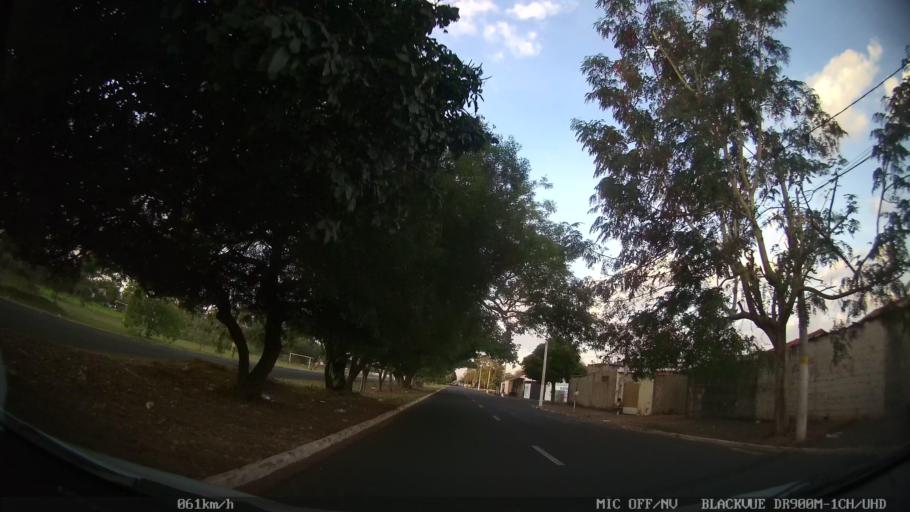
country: BR
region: Sao Paulo
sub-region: Ribeirao Preto
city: Ribeirao Preto
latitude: -21.1272
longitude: -47.8319
